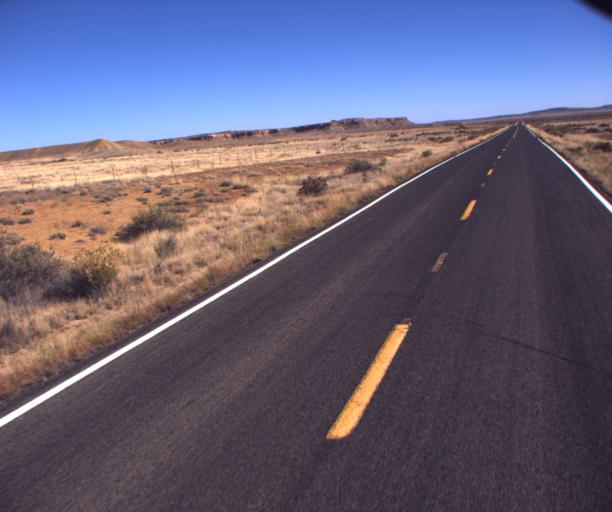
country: US
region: Arizona
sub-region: Navajo County
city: First Mesa
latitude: 35.9780
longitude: -110.7474
